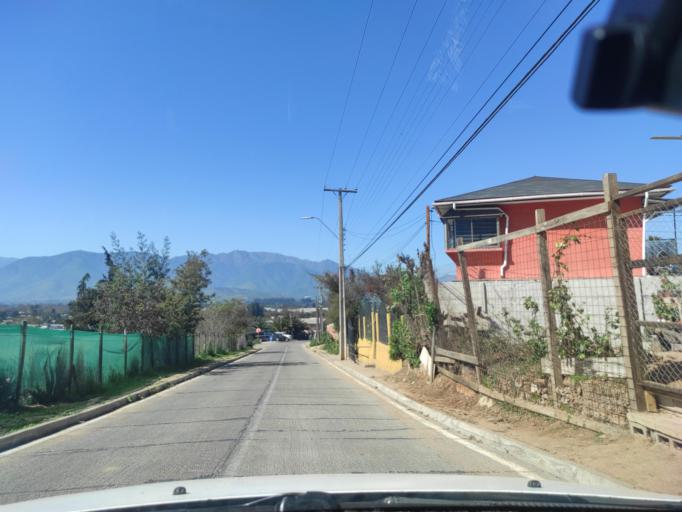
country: CL
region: Valparaiso
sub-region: Provincia de Marga Marga
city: Limache
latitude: -32.9919
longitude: -71.2262
